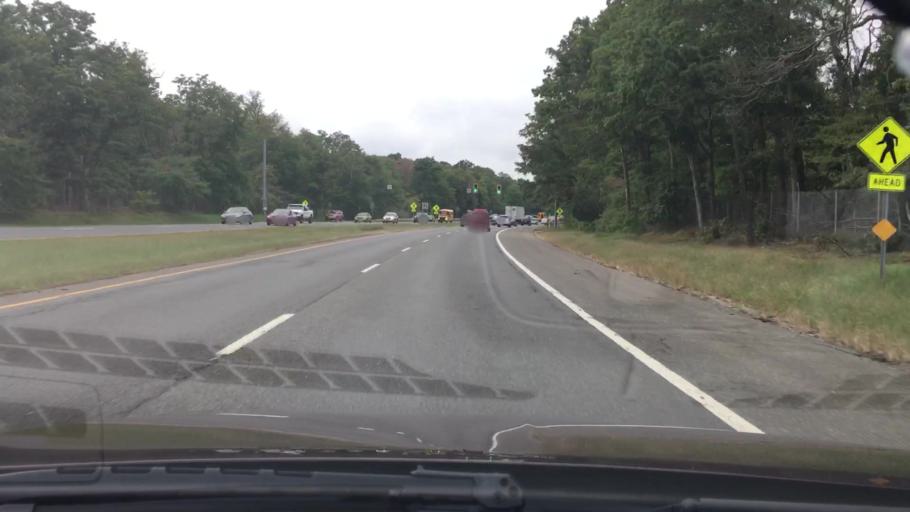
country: US
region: New York
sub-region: Suffolk County
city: Islandia
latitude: 40.7919
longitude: -73.1634
